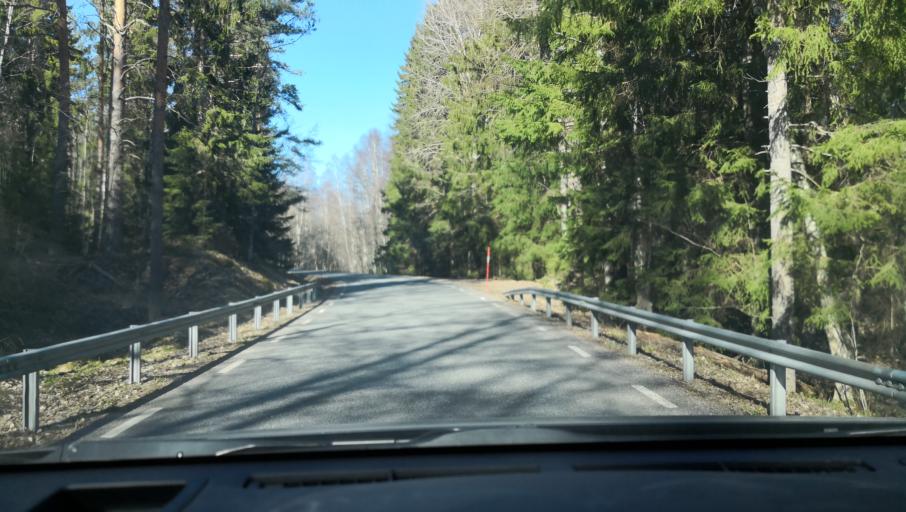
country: SE
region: Vaestmanland
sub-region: Sala Kommun
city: Sala
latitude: 59.9786
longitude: 16.4738
